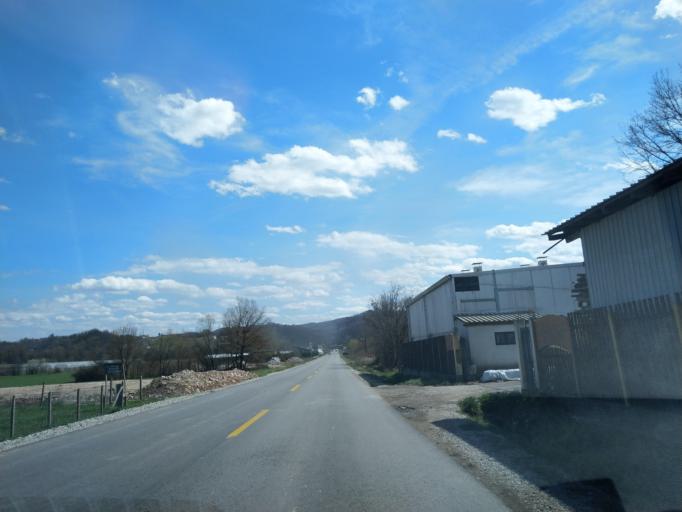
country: RS
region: Central Serbia
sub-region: Zlatiborski Okrug
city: Arilje
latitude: 43.7935
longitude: 20.1007
